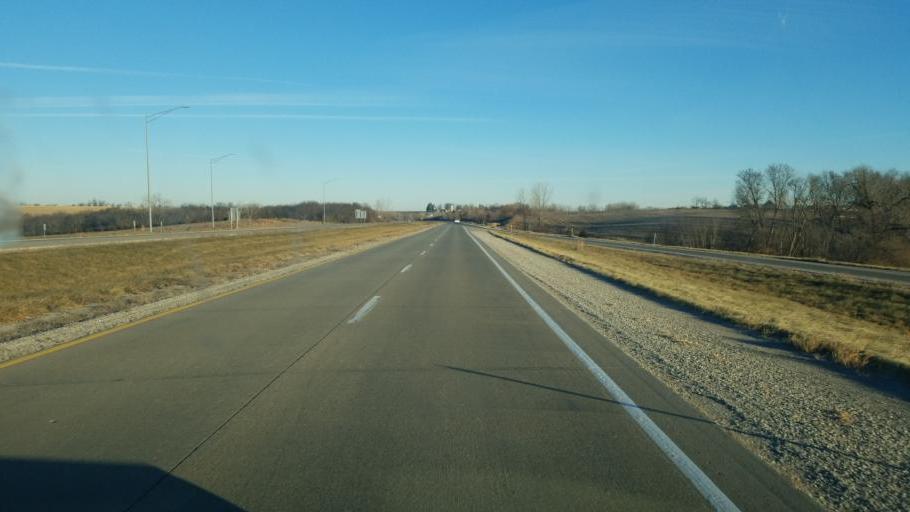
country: US
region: Iowa
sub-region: Mahaska County
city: Oskaloosa
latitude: 41.2992
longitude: -92.6746
